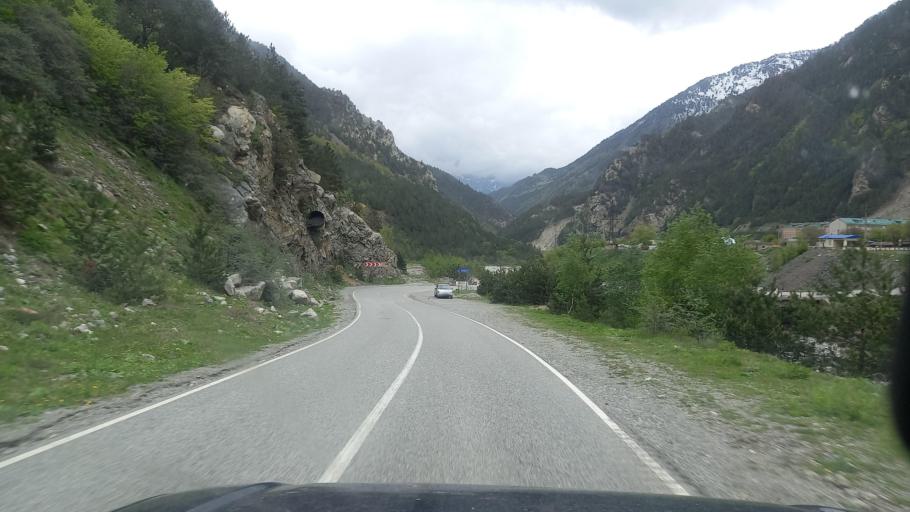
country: RU
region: North Ossetia
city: Mizur
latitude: 42.7939
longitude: 44.0039
